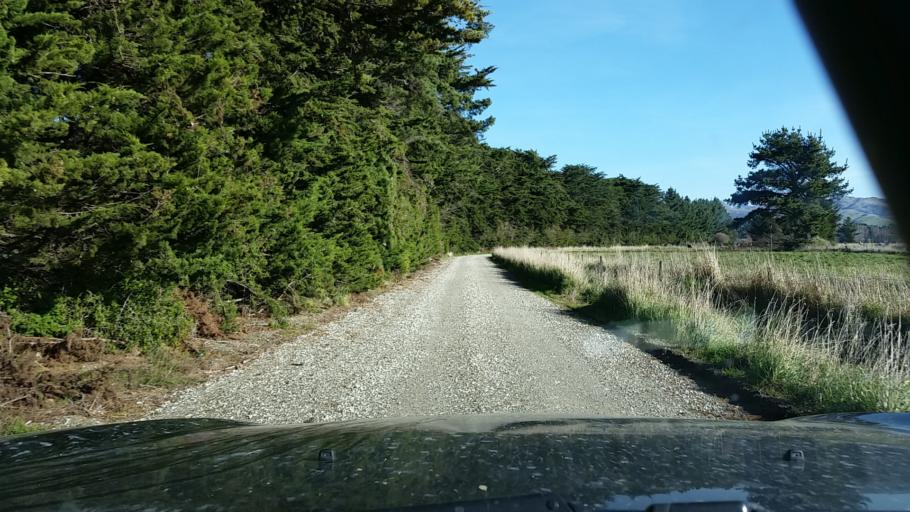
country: NZ
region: Marlborough
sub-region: Marlborough District
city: Blenheim
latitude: -41.8260
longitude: 174.1556
